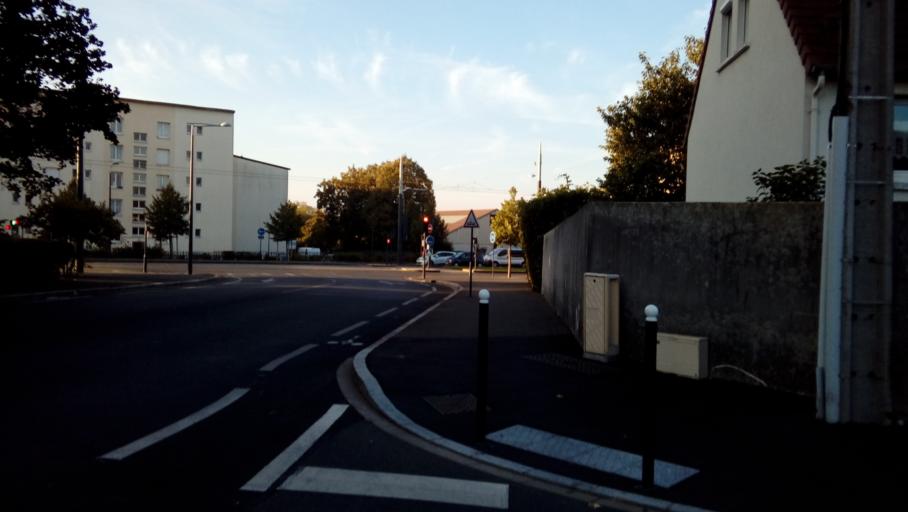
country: FR
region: Centre
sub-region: Departement du Loiret
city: Saint-Jean-le-Blanc
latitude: 47.9120
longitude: 1.9262
